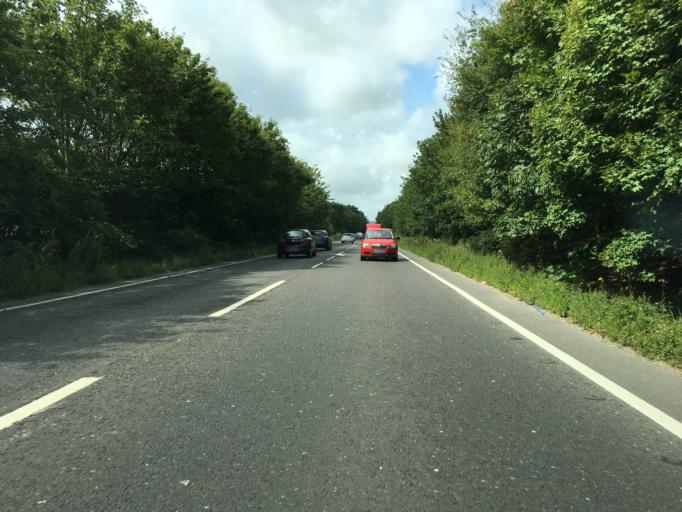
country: GB
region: England
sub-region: East Sussex
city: Ringmer
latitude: 50.8530
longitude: 0.0649
